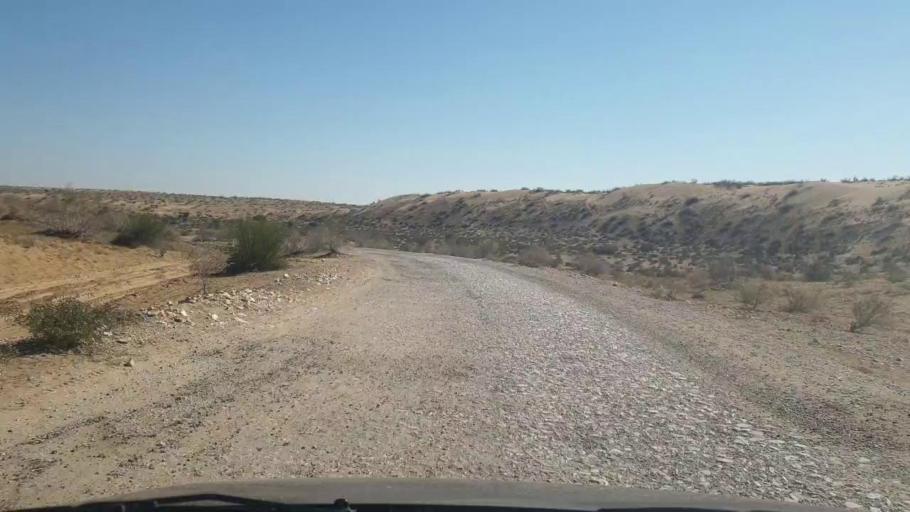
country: PK
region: Sindh
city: Bozdar
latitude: 27.0137
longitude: 68.7384
